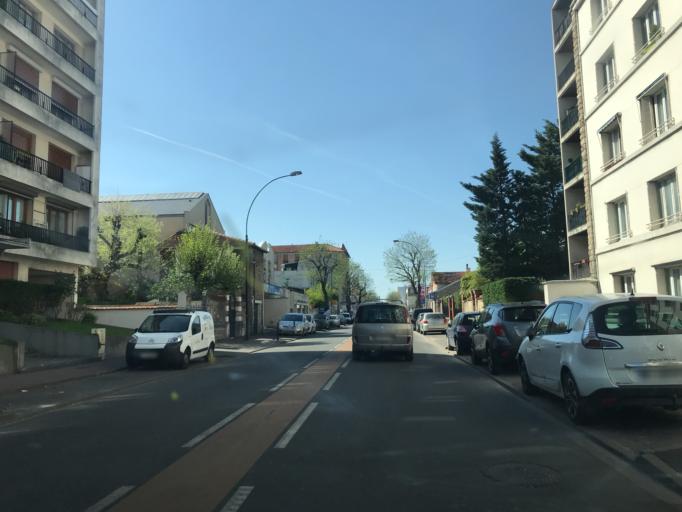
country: FR
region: Ile-de-France
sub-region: Departement du Val-de-Marne
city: Saint-Maur-des-Fosses
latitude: 48.7985
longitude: 2.5014
